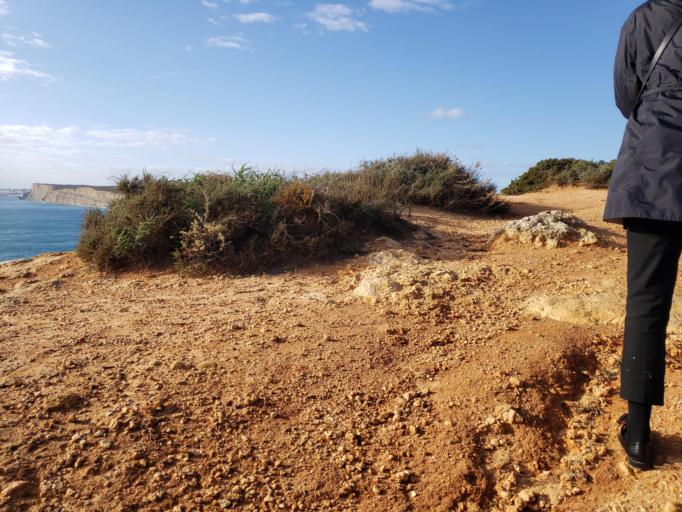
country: PT
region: Faro
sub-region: Lagos
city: Lagos
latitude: 37.0806
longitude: -8.6706
